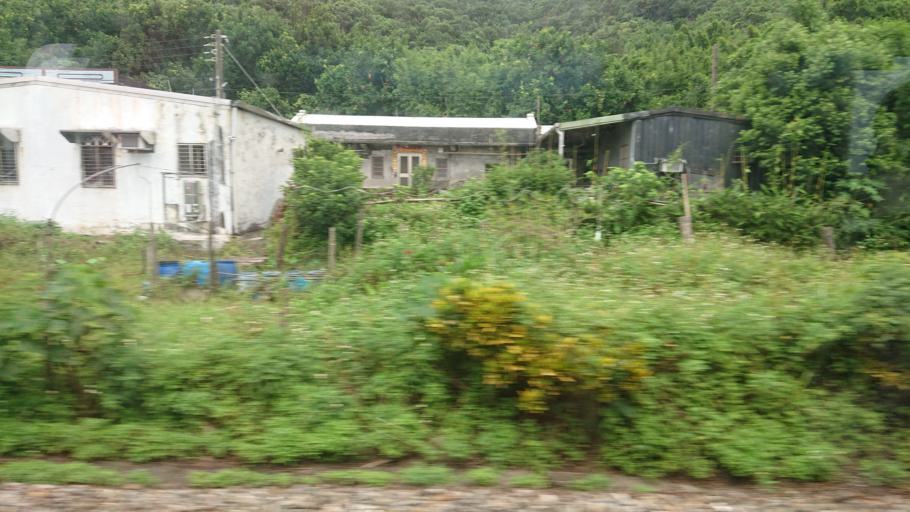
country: TW
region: Taiwan
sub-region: Keelung
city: Keelung
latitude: 24.9582
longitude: 121.9176
